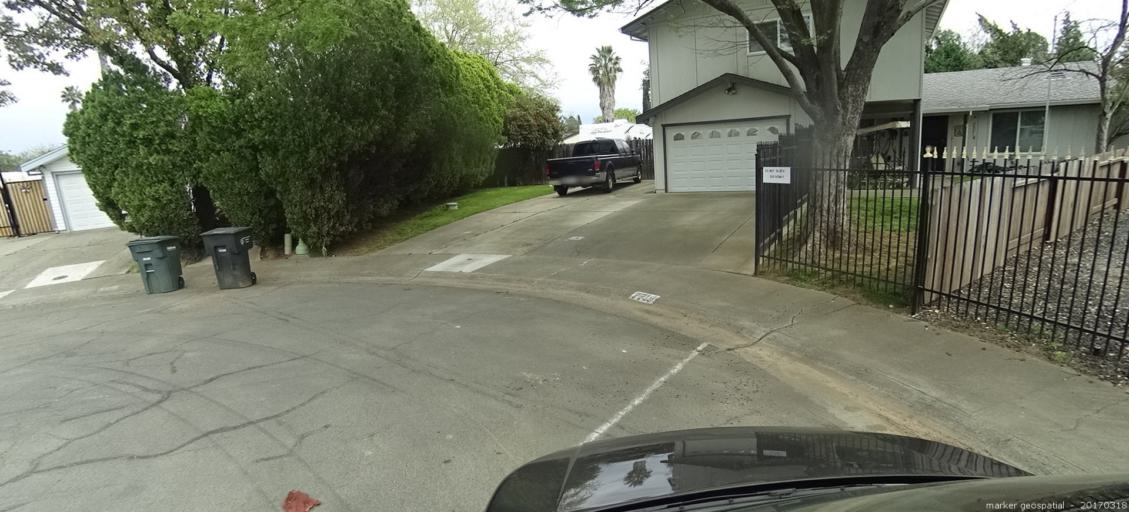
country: US
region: California
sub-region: Sacramento County
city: Parkway
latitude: 38.4775
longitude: -121.4382
